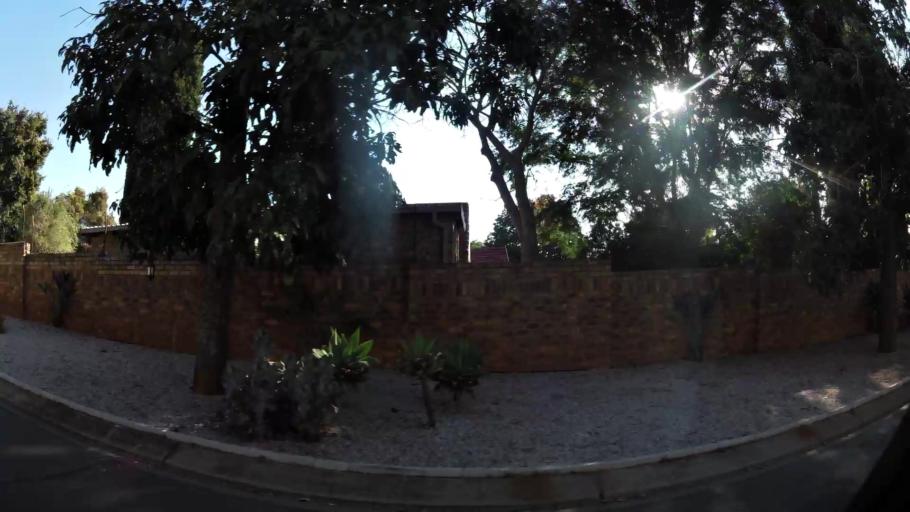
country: ZA
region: Gauteng
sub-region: City of Johannesburg Metropolitan Municipality
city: Roodepoort
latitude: -26.0902
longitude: 27.9504
